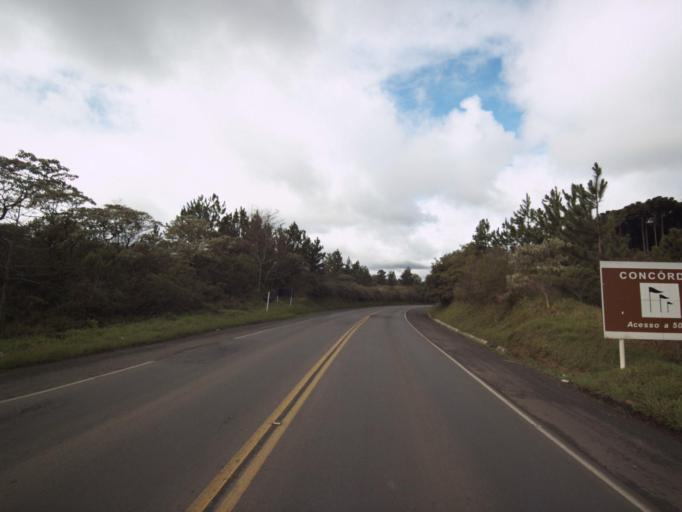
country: BR
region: Santa Catarina
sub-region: Concordia
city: Concordia
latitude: -27.2184
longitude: -51.9497
